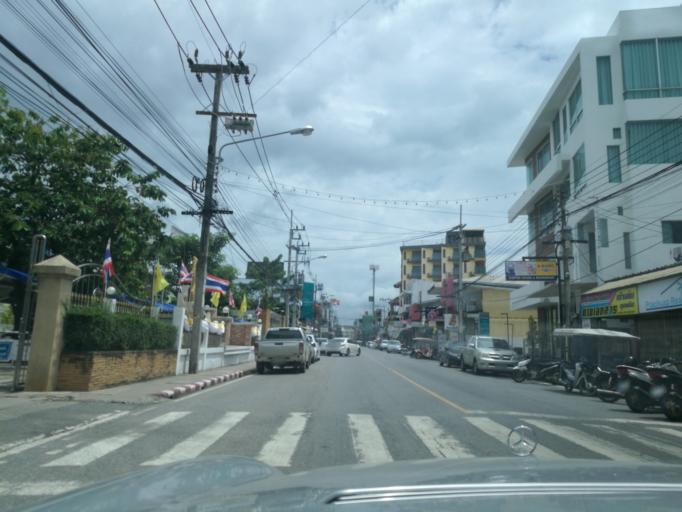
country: TH
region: Prachuap Khiri Khan
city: Prachuap Khiri Khan
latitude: 11.8000
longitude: 99.7988
